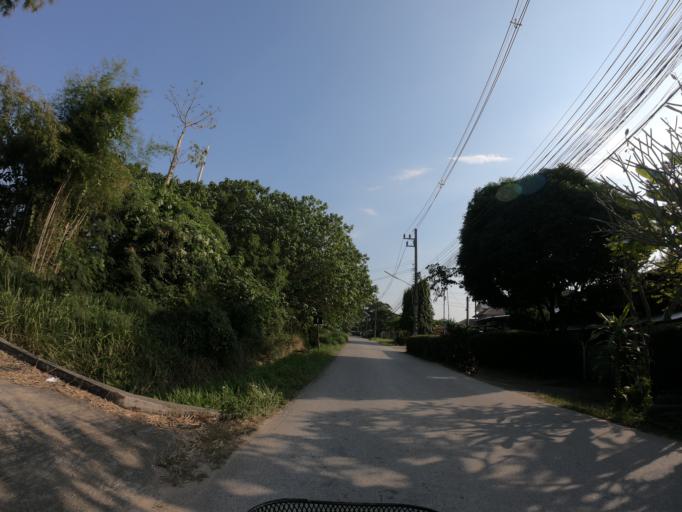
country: TH
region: Chiang Mai
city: Chiang Mai
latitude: 18.8348
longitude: 98.9884
